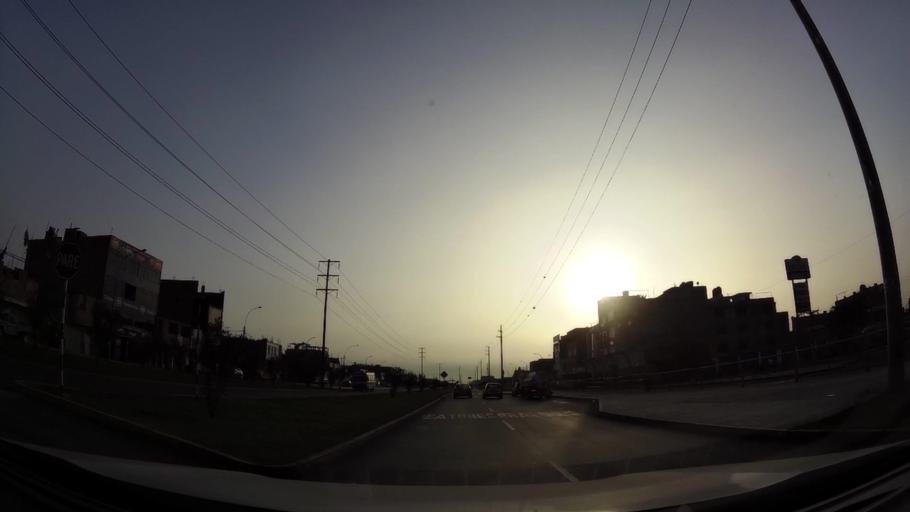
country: PE
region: Lima
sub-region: Lima
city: Independencia
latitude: -11.9895
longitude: -77.1014
